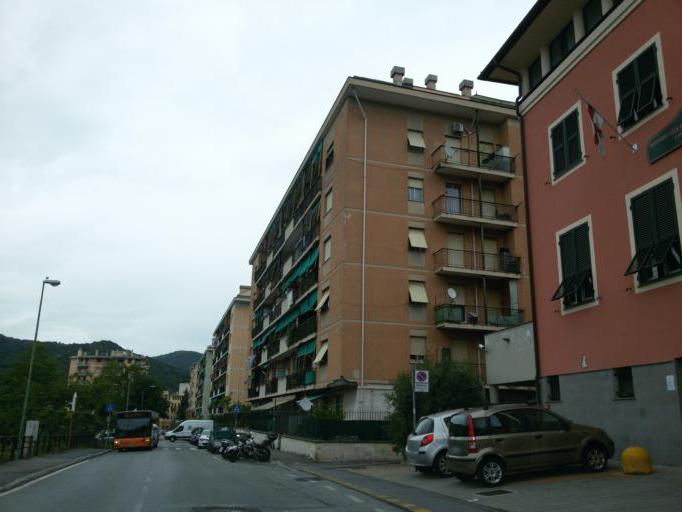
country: IT
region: Liguria
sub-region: Provincia di Genova
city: Piccarello
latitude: 44.4366
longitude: 8.9660
